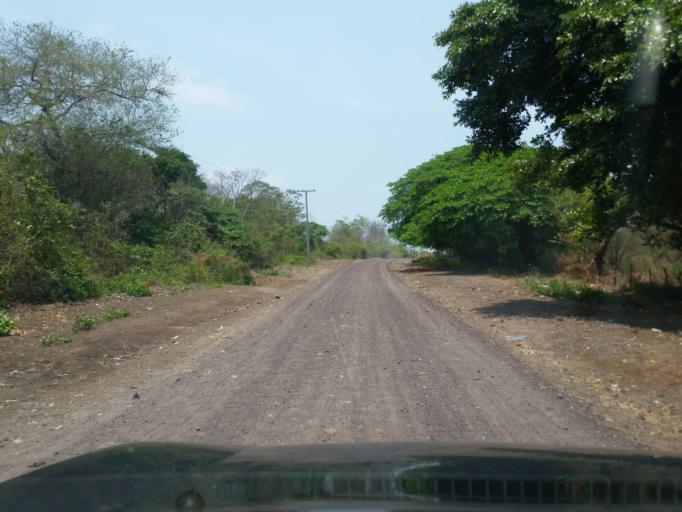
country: NI
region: Granada
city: Granada
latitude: 11.9065
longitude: -85.9430
